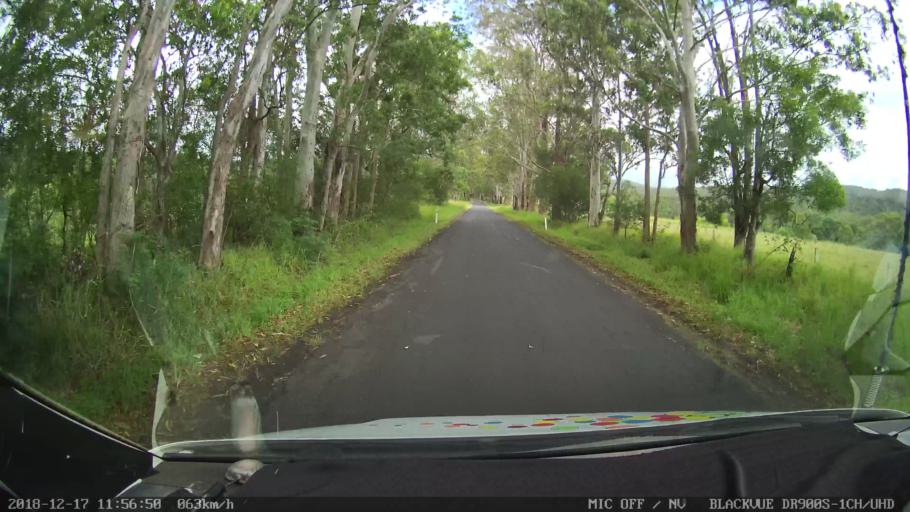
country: AU
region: New South Wales
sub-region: Kyogle
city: Kyogle
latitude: -28.5445
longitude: 152.5784
